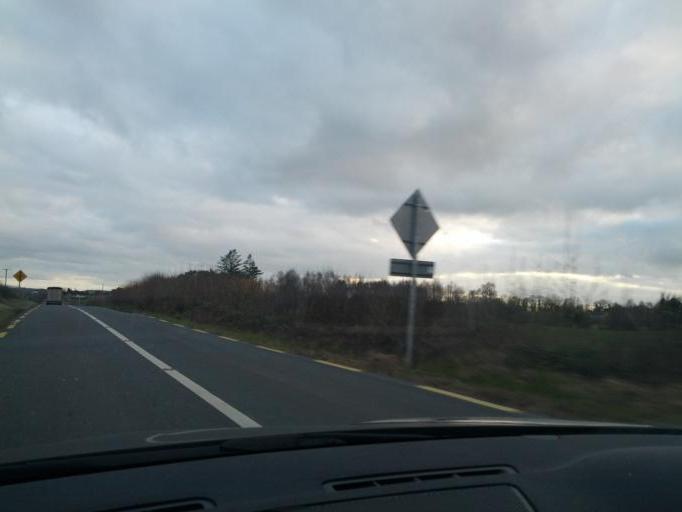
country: IE
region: Leinster
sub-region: Uibh Fhaili
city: Birr
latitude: 53.1598
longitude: -7.8828
